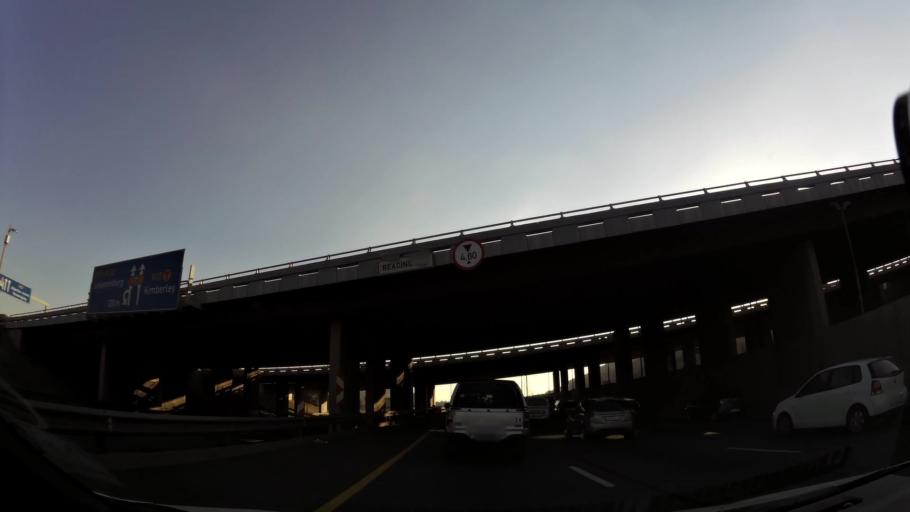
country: ZA
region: Gauteng
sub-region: City of Johannesburg Metropolitan Municipality
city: Johannesburg
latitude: -26.2640
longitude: 28.0963
